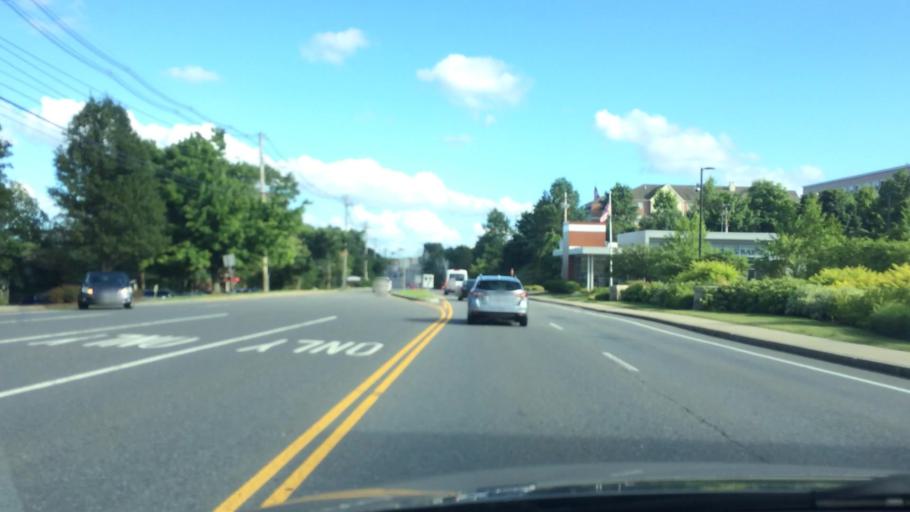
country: US
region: Massachusetts
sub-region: Middlesex County
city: Burlington
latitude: 42.4879
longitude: -71.2222
